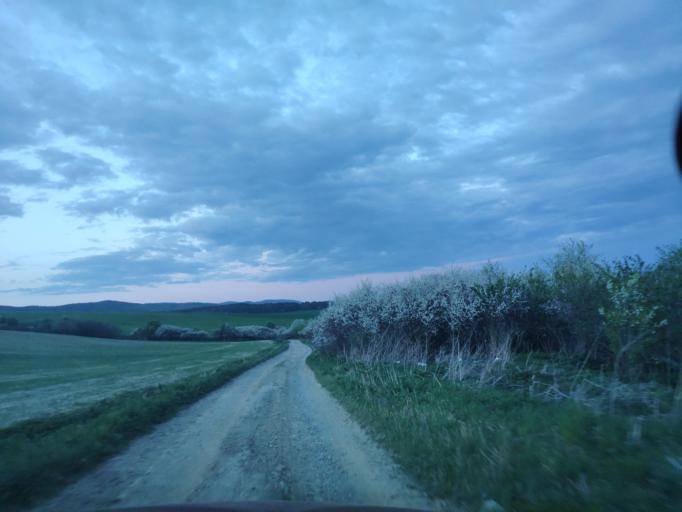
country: SK
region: Presovsky
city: Lipany
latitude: 49.1801
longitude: 20.8392
